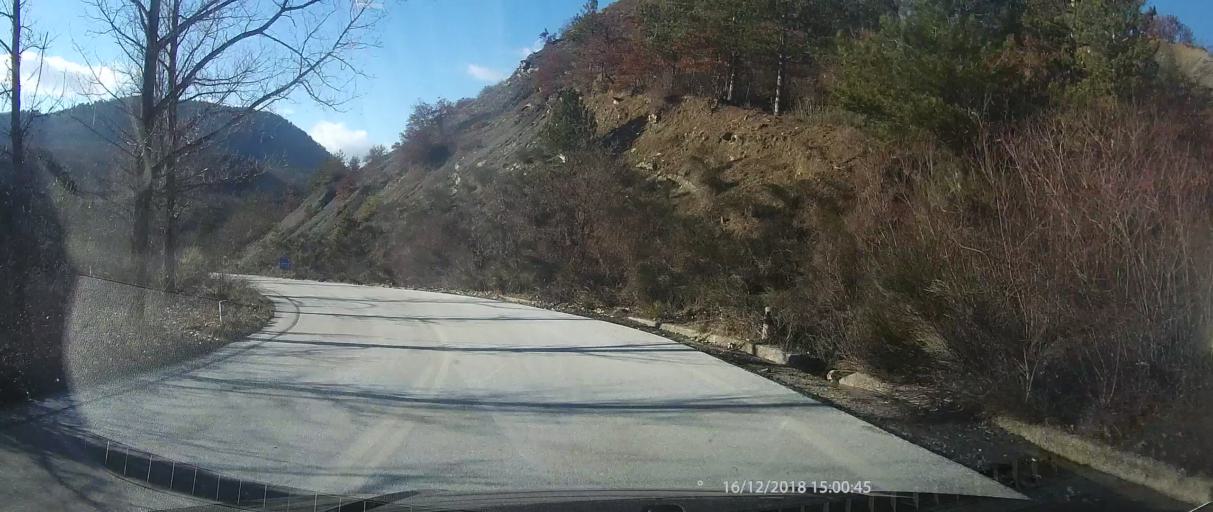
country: GR
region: West Macedonia
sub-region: Nomos Kastorias
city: Nestorio
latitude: 40.2196
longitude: 21.0144
